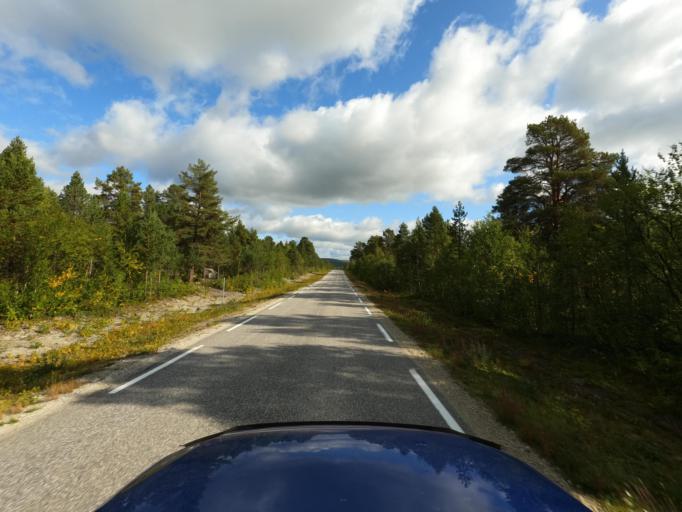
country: NO
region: Finnmark Fylke
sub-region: Karasjok
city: Karasjohka
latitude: 69.4325
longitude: 24.9720
